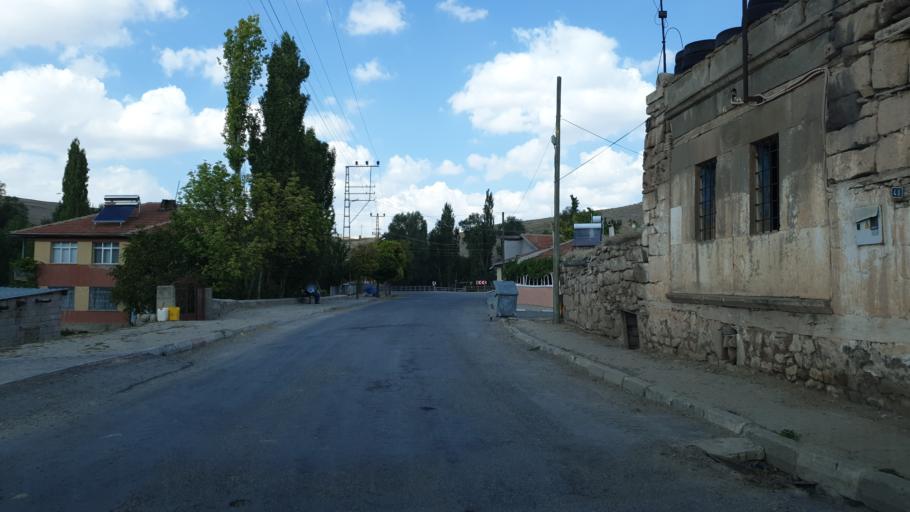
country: TR
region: Kayseri
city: Felahiye
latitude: 39.0928
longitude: 35.5631
